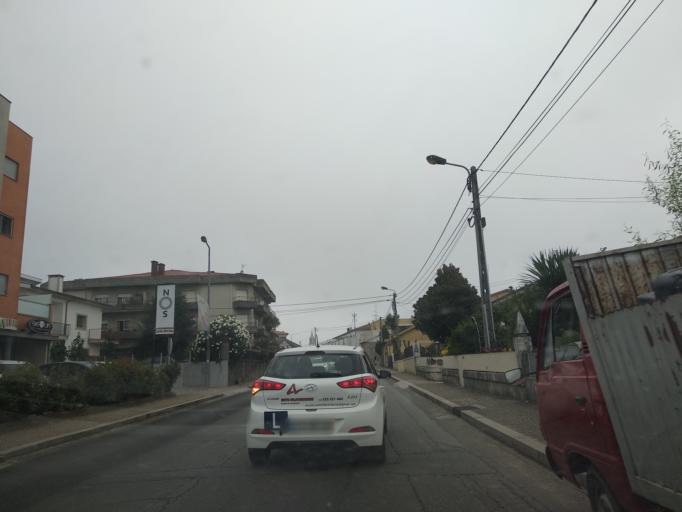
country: PT
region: Braga
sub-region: Vila Verde
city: Vila Verde
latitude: 41.6432
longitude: -8.4353
